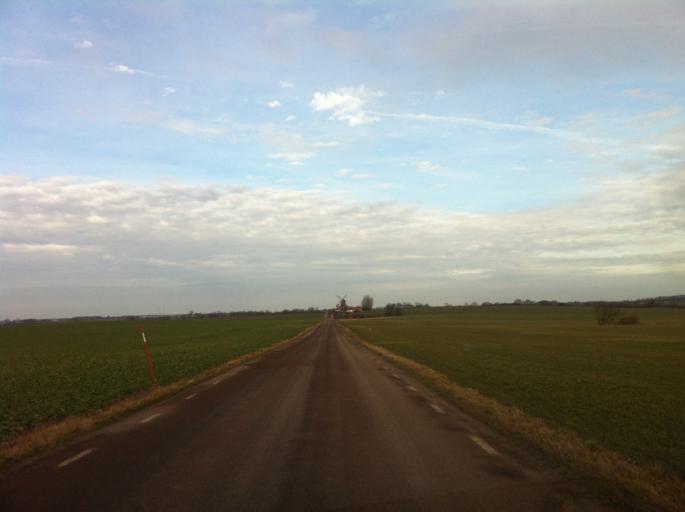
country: SE
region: Skane
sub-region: Landskrona
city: Asmundtorp
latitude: 55.9099
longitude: 13.0051
